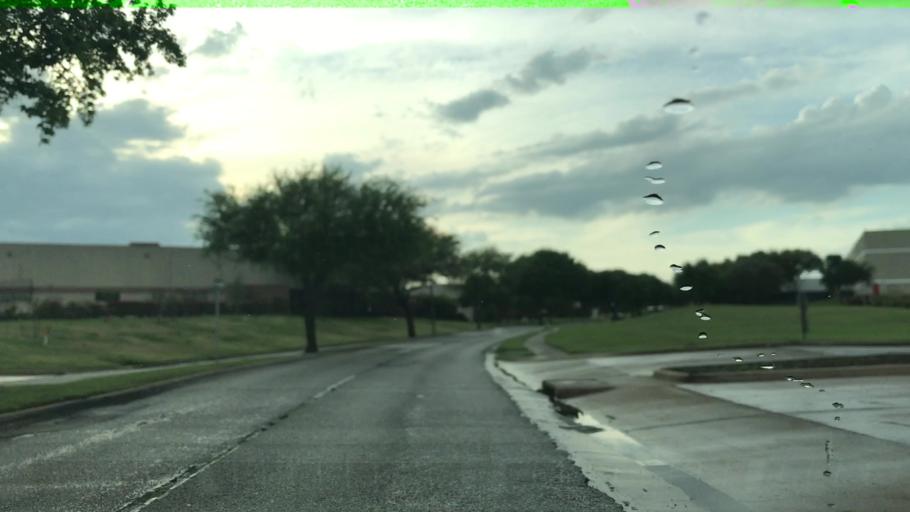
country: US
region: Texas
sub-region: Dallas County
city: Irving
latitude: 32.8690
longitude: -96.9792
